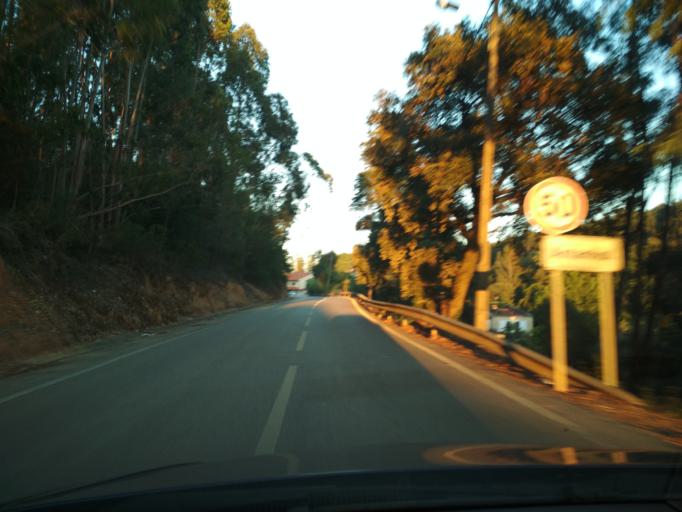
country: PT
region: Coimbra
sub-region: Condeixa-A-Nova
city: Condeixa-a-Nova
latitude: 40.1678
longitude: -8.4749
